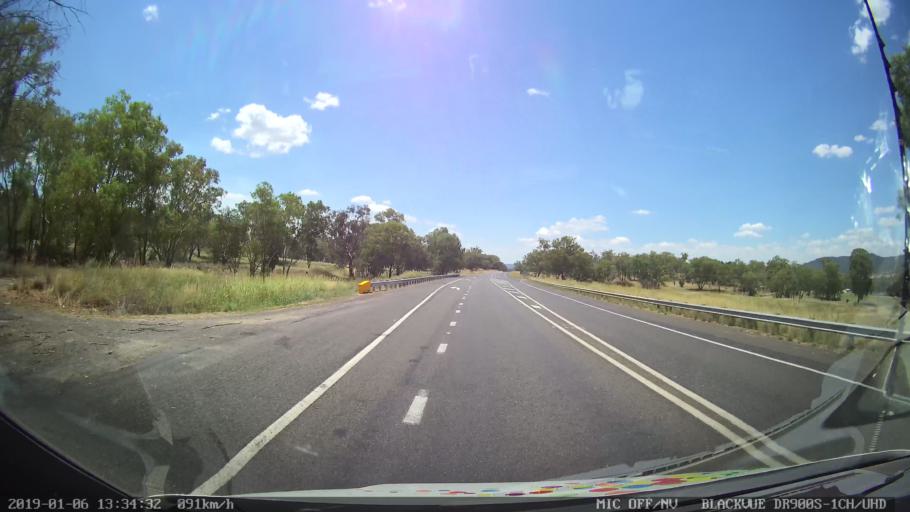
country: AU
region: New South Wales
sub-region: Tamworth Municipality
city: Kootingal
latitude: -31.0878
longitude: 151.0170
